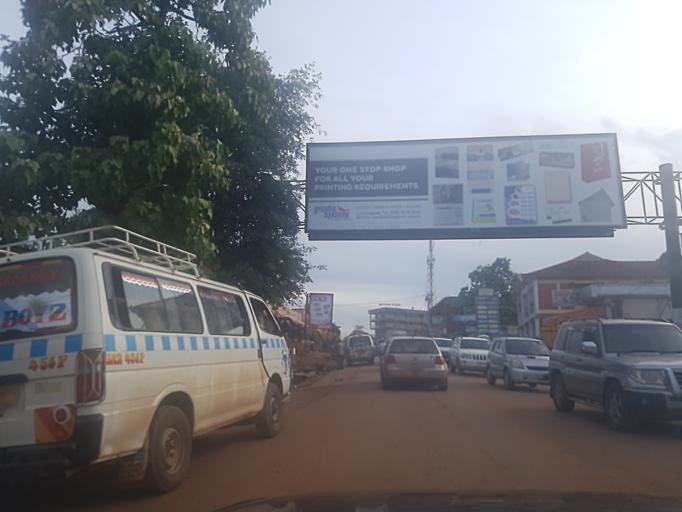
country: UG
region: Central Region
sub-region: Wakiso District
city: Bweyogerere
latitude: 0.3800
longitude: 32.6465
